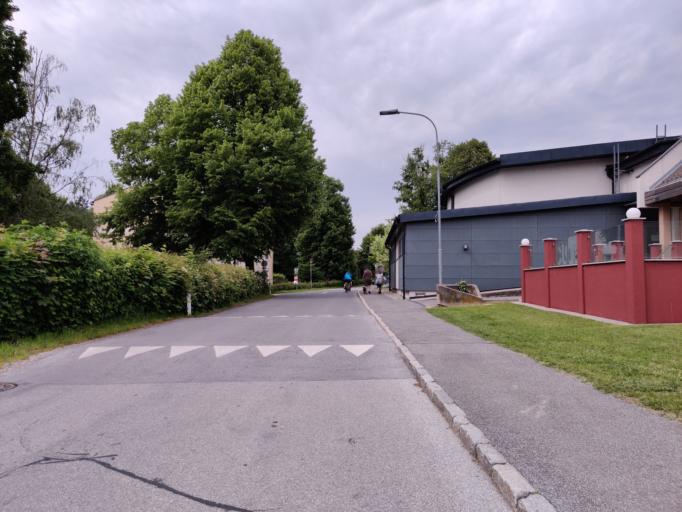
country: AT
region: Styria
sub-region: Politischer Bezirk Graz-Umgebung
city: Werndorf
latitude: 46.9216
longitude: 15.4827
